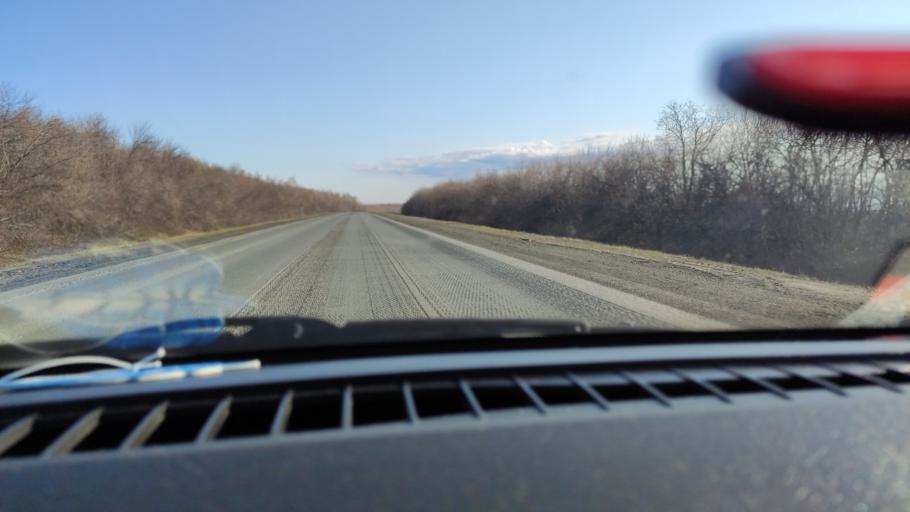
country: RU
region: Saratov
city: Dukhovnitskoye
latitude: 52.6481
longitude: 48.1974
